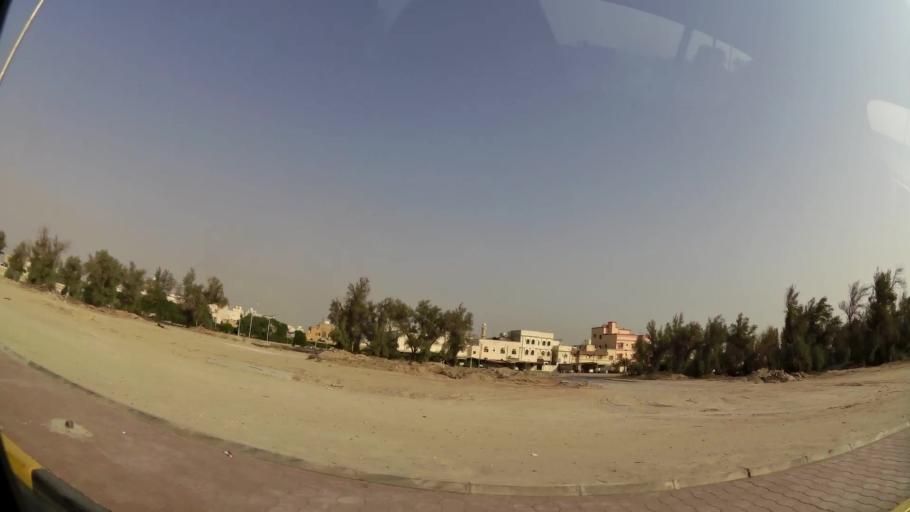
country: KW
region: Al Asimah
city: Ar Rabiyah
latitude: 29.3117
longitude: 47.8130
